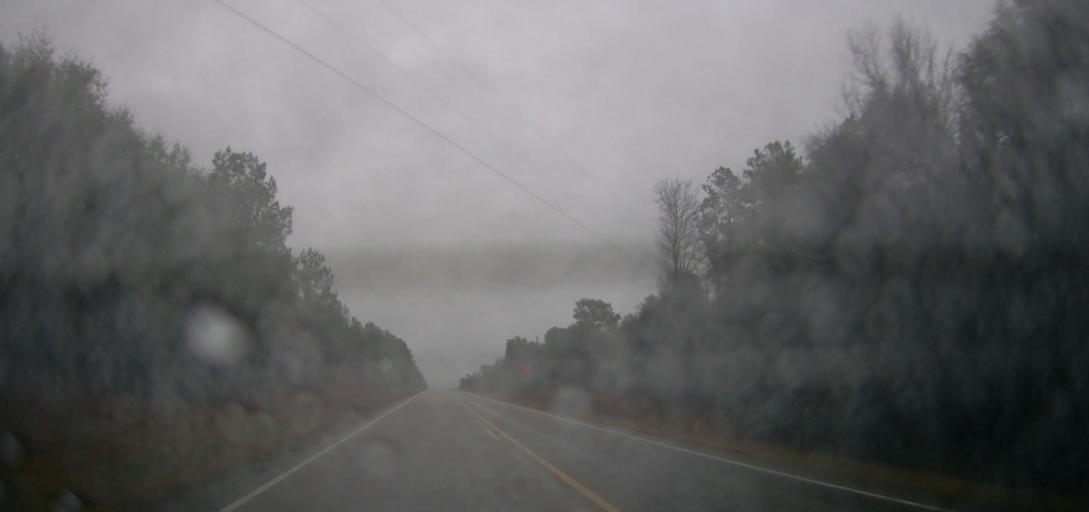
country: US
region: Alabama
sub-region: Autauga County
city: Pine Level
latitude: 32.5532
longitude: -86.6568
